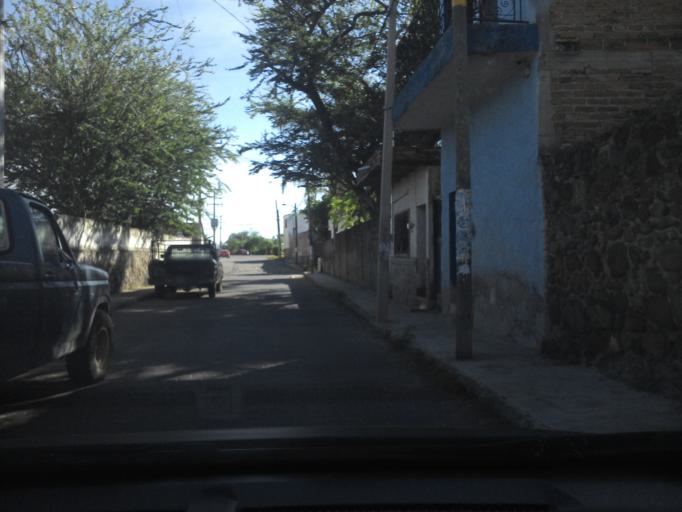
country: MX
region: Jalisco
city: Teuchitlan
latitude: 20.6820
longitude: -103.8475
